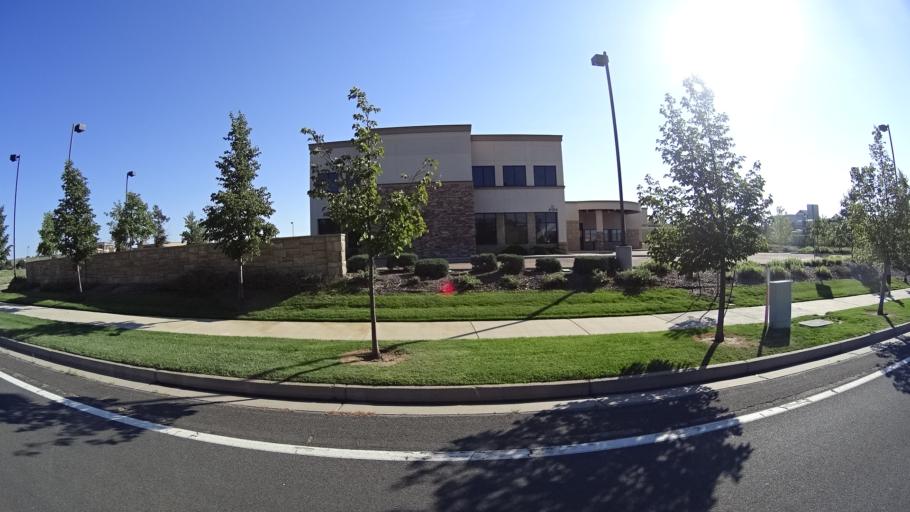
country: US
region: Colorado
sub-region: El Paso County
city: Black Forest
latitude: 38.9714
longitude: -104.7521
